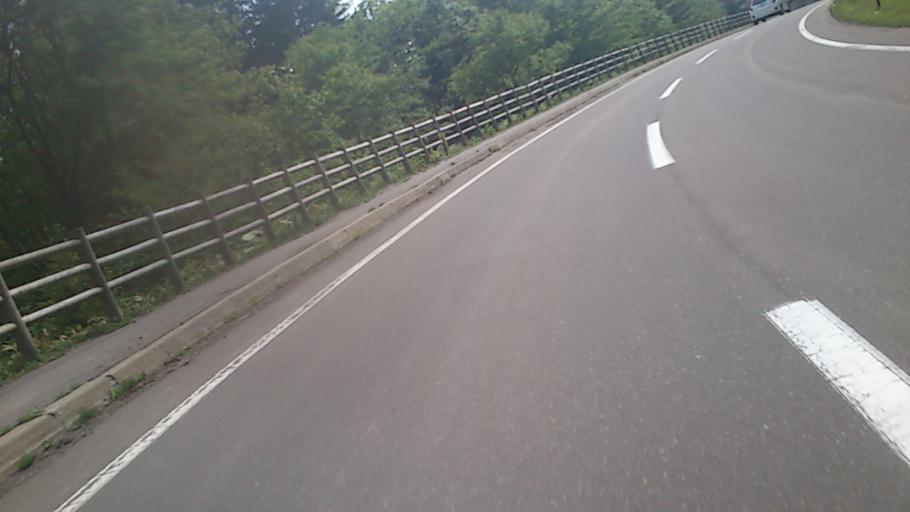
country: JP
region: Hokkaido
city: Kitami
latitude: 43.3933
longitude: 143.9777
